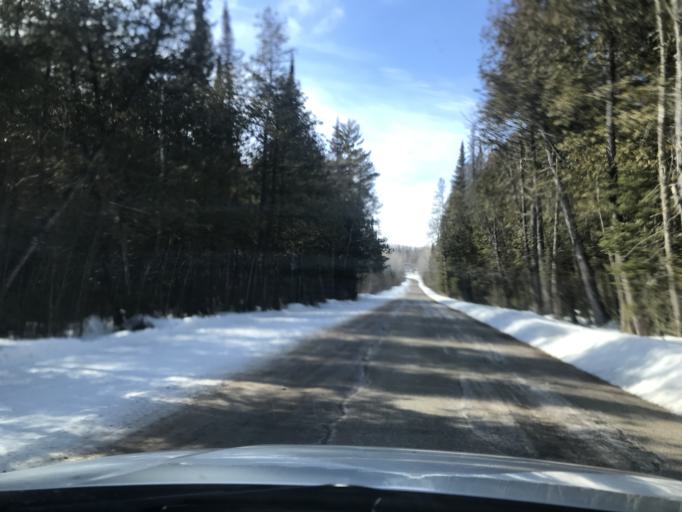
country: US
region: Wisconsin
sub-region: Marinette County
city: Peshtigo
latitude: 45.3007
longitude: -87.8312
